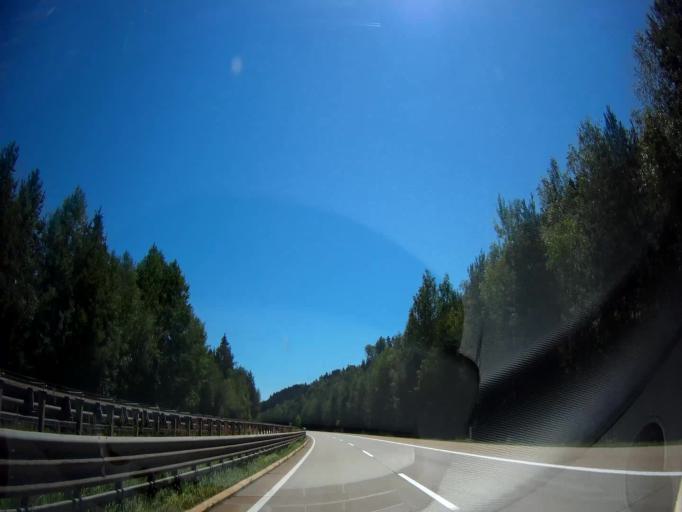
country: AT
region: Carinthia
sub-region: Politischer Bezirk Spittal an der Drau
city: Millstatt
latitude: 46.7468
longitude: 13.5775
